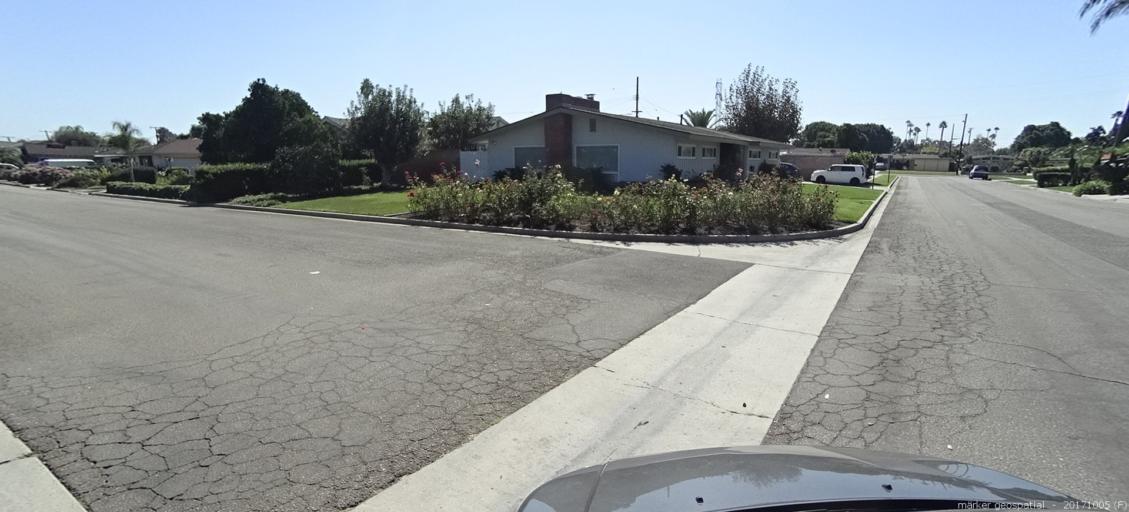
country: US
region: California
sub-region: Orange County
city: Stanton
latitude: 33.7990
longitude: -117.9714
